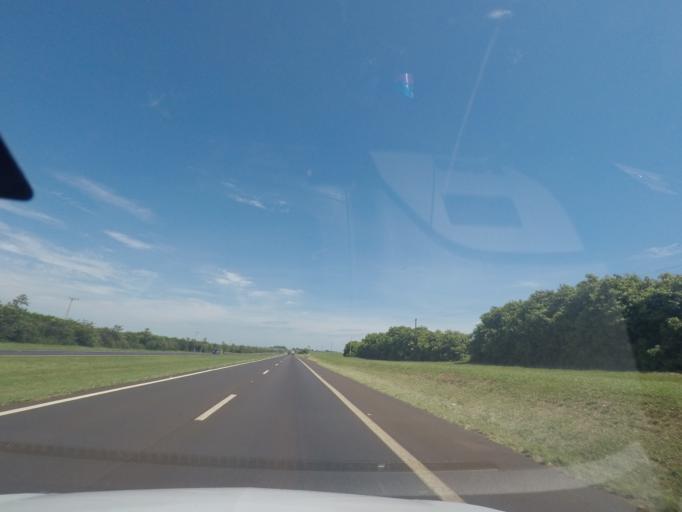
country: BR
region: Sao Paulo
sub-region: Araraquara
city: Araraquara
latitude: -21.8605
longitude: -48.1196
